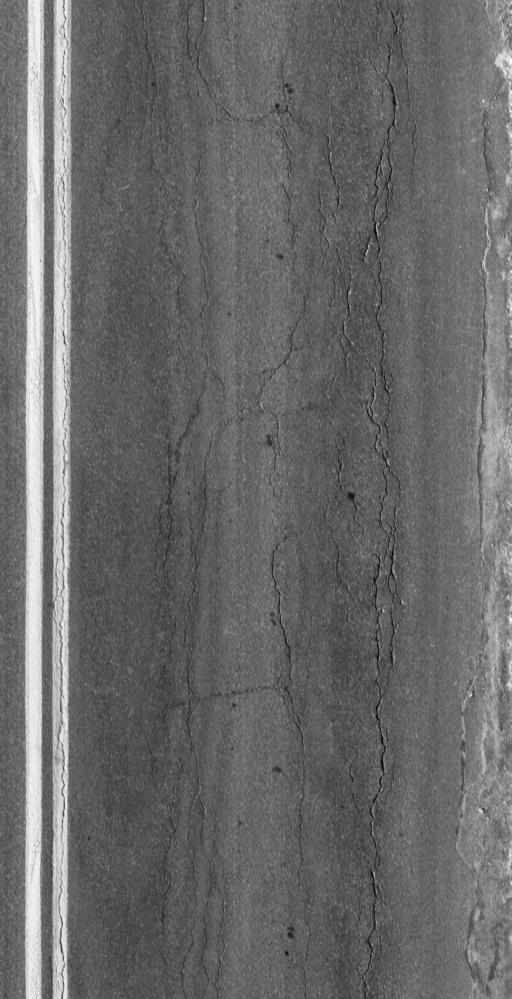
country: US
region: Vermont
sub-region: Chittenden County
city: Burlington
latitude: 44.3652
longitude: -73.2234
